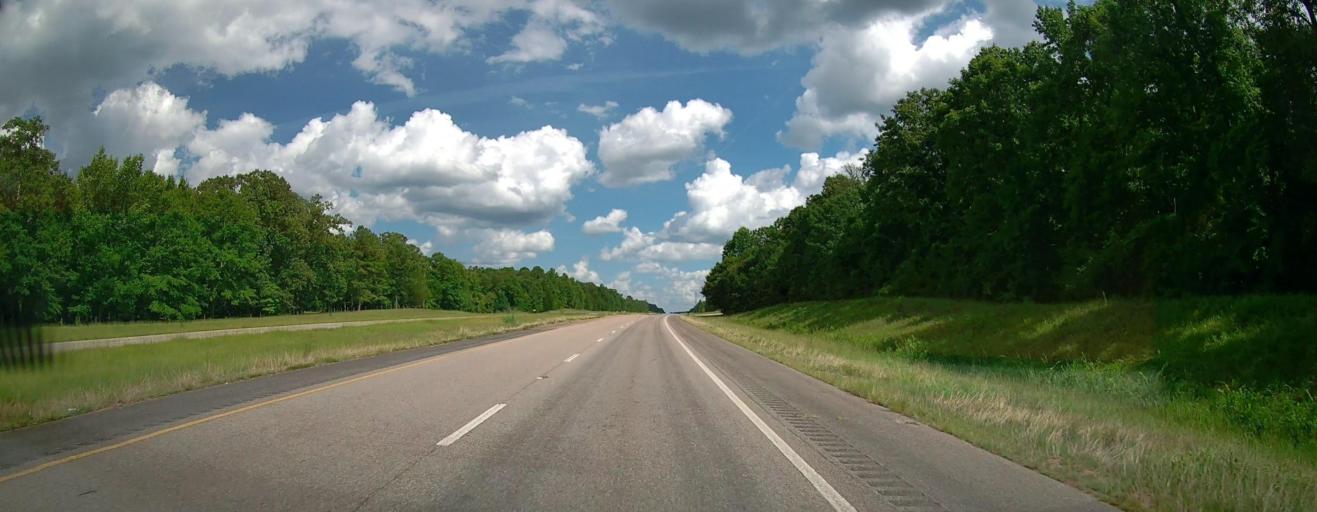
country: US
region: Mississippi
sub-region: Lowndes County
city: New Hope
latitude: 33.4650
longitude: -88.2301
